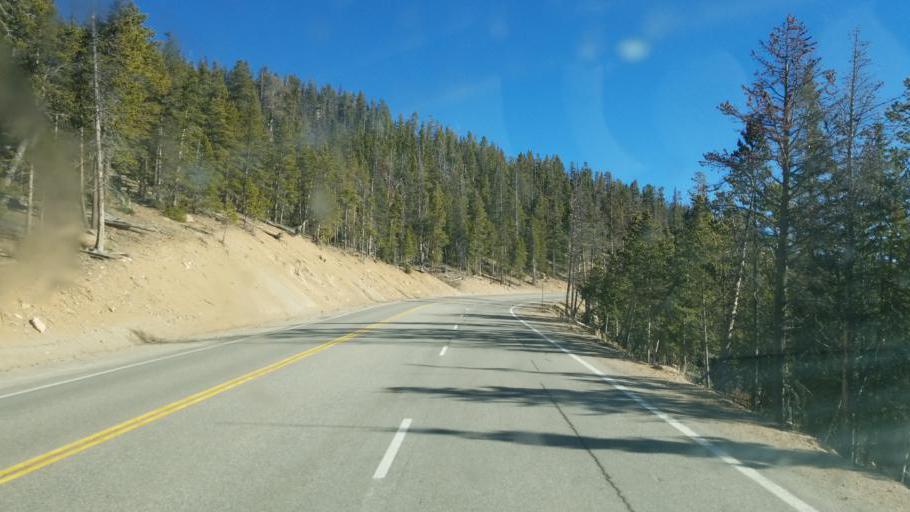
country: US
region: Colorado
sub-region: Chaffee County
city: Salida
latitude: 38.4851
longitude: -106.3323
